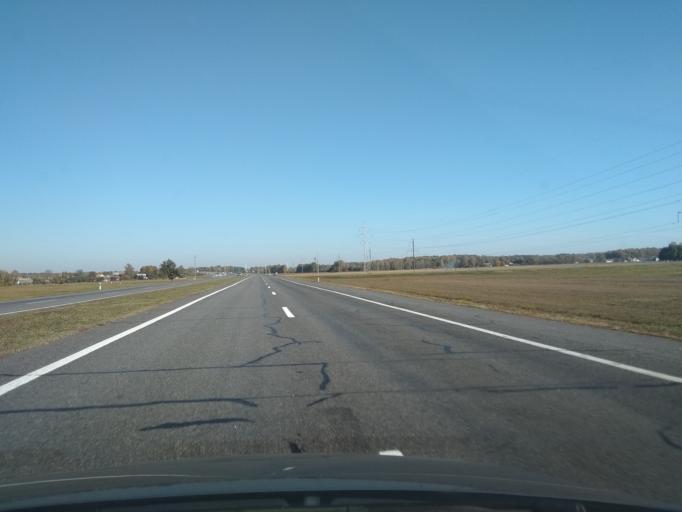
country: BY
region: Brest
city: Horad Kobryn
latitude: 52.1973
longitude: 24.4132
